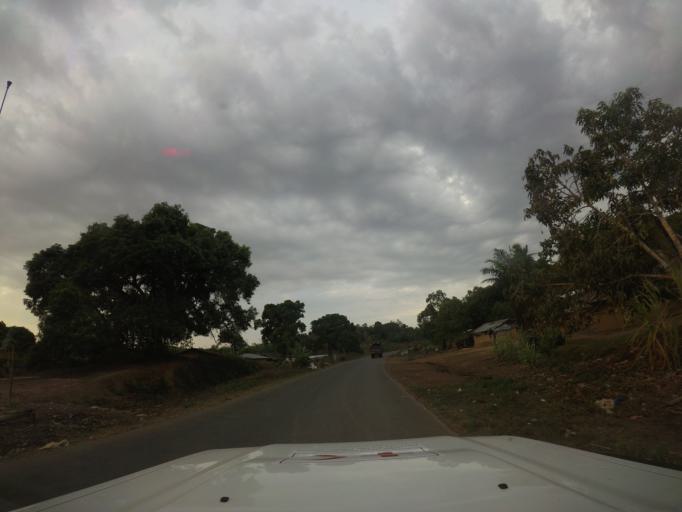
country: LR
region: Bomi
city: Tubmanburg
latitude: 6.7849
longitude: -10.8454
